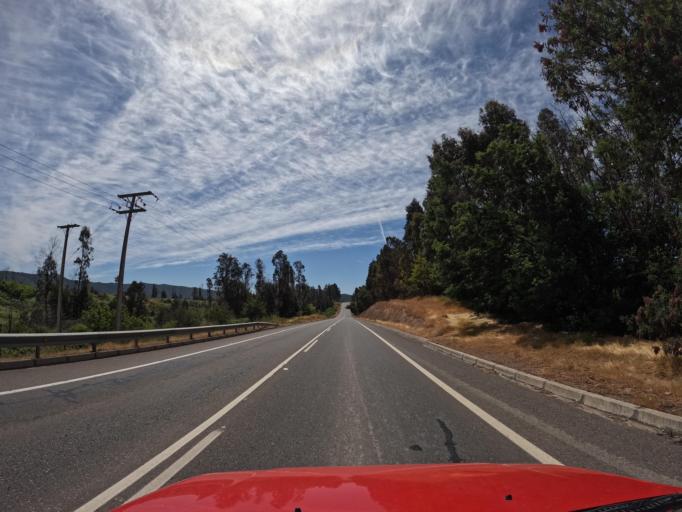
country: CL
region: Maule
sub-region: Provincia de Talca
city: Talca
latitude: -35.2872
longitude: -71.5309
